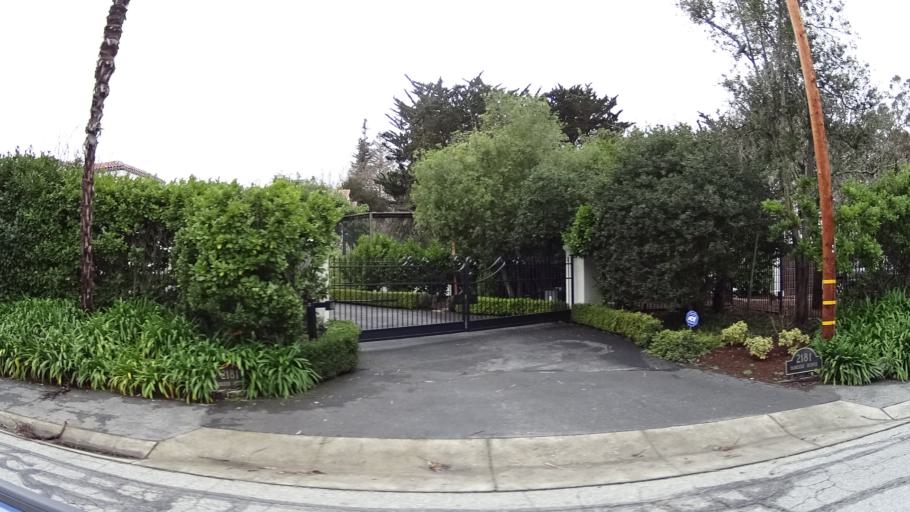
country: US
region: California
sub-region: San Mateo County
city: Burlingame
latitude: 37.5691
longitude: -122.3578
